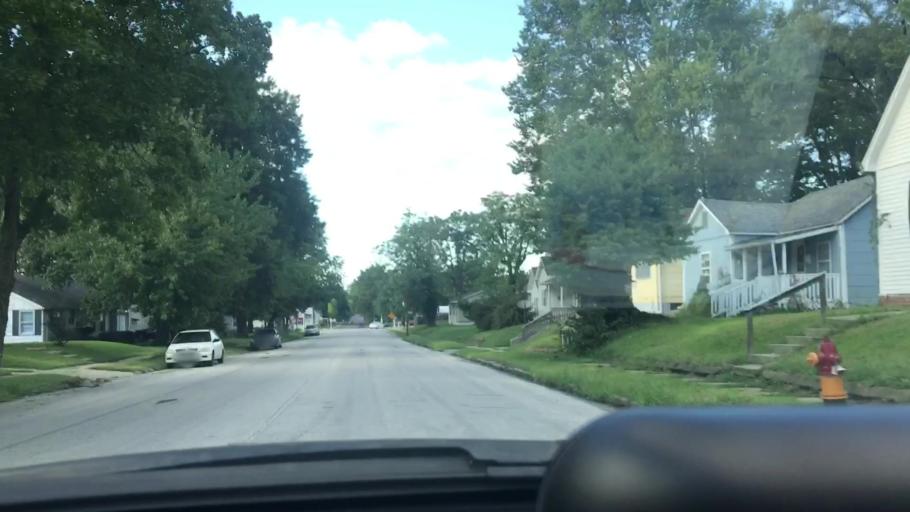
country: US
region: Missouri
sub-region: Pettis County
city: Sedalia
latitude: 38.6961
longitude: -93.2368
